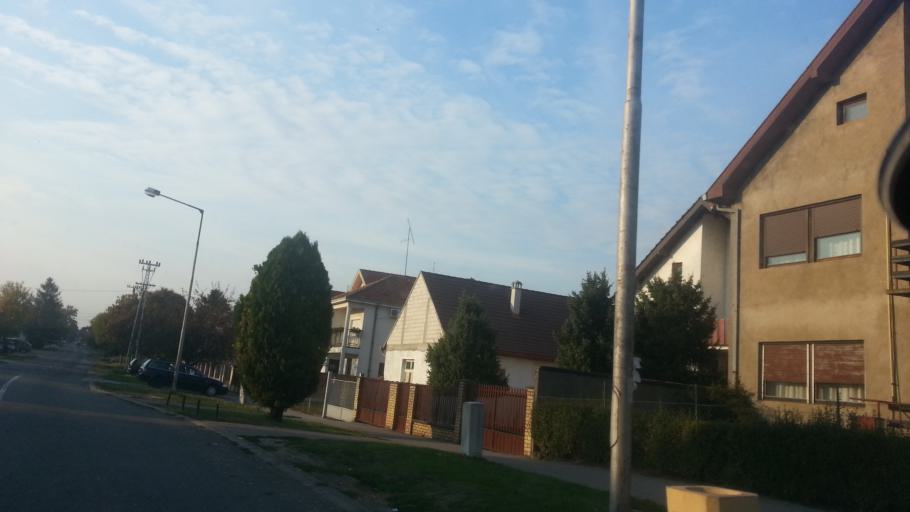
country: RS
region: Autonomna Pokrajina Vojvodina
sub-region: Sremski Okrug
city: Ingija
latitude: 45.0441
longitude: 20.0752
